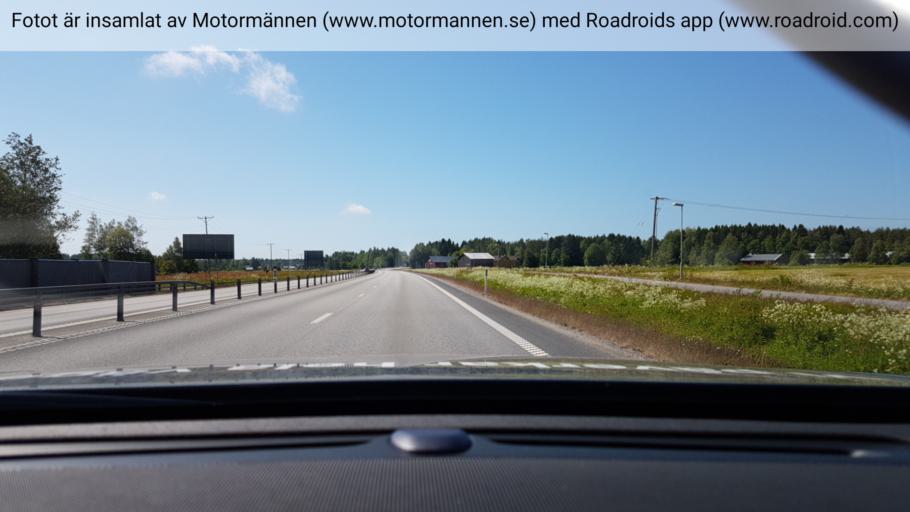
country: SE
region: Vaesterbotten
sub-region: Umea Kommun
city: Roback
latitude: 63.7752
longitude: 20.1868
